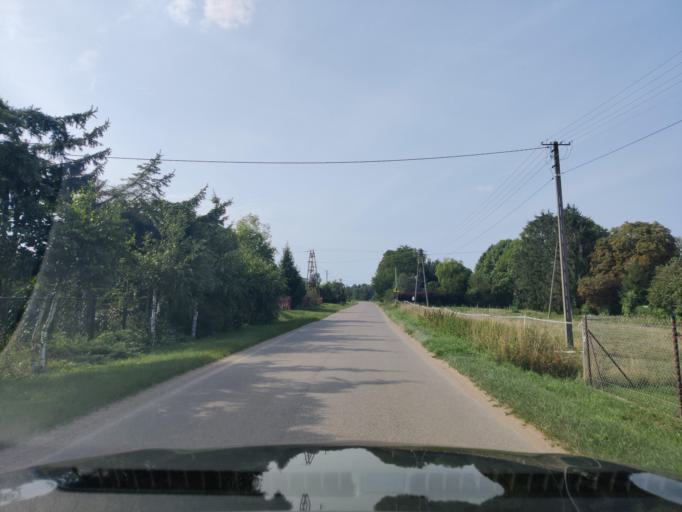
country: PL
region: Masovian Voivodeship
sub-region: Powiat pultuski
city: Obryte
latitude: 52.7666
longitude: 21.2835
